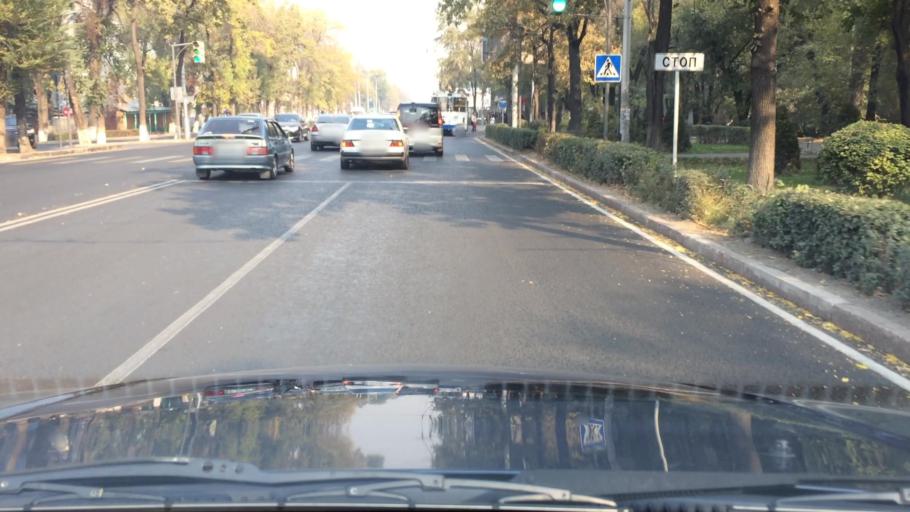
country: KG
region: Chuy
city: Bishkek
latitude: 42.8534
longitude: 74.5866
